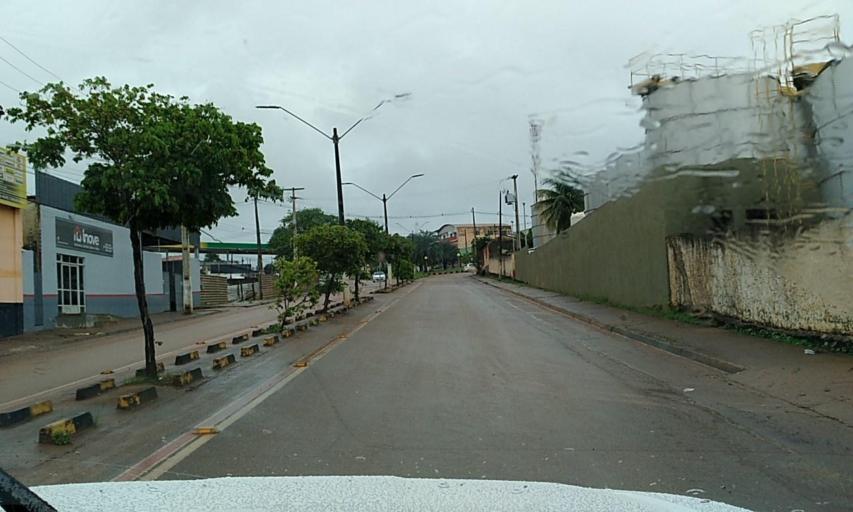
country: BR
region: Para
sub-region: Altamira
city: Altamira
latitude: -3.2125
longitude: -52.2312
